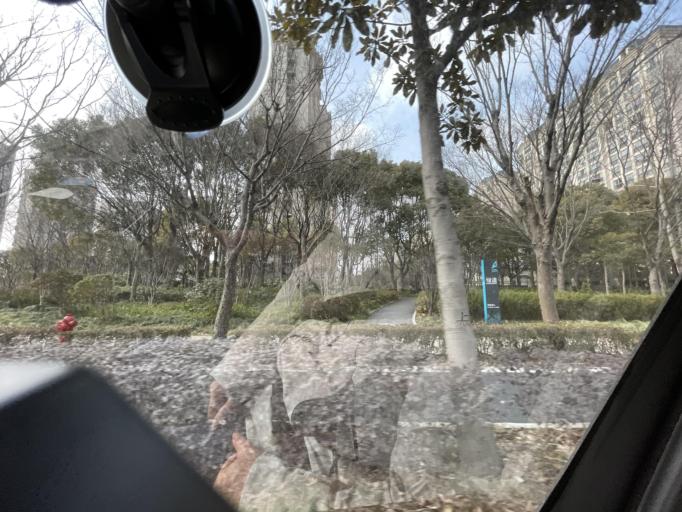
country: CN
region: Shanghai Shi
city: Yangpu
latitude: 31.3282
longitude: 121.5021
